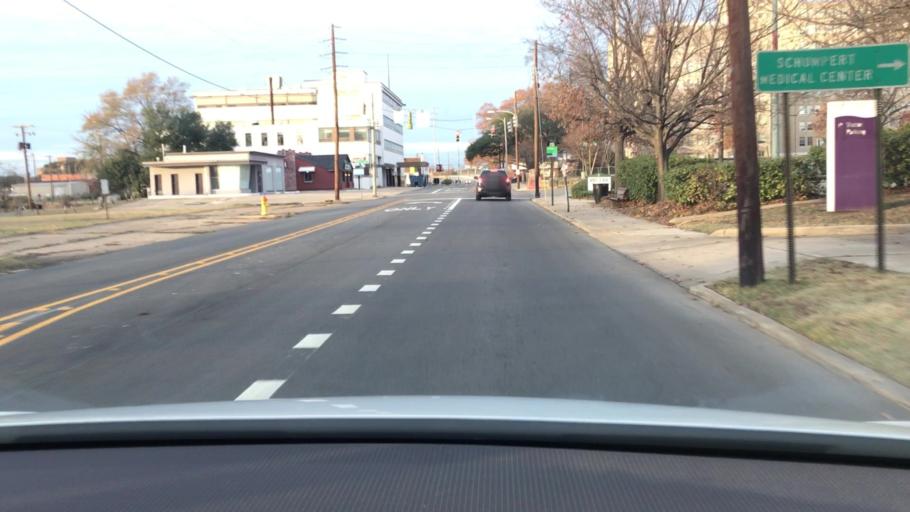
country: US
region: Louisiana
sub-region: Bossier Parish
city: Bossier City
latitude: 32.4955
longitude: -93.7524
